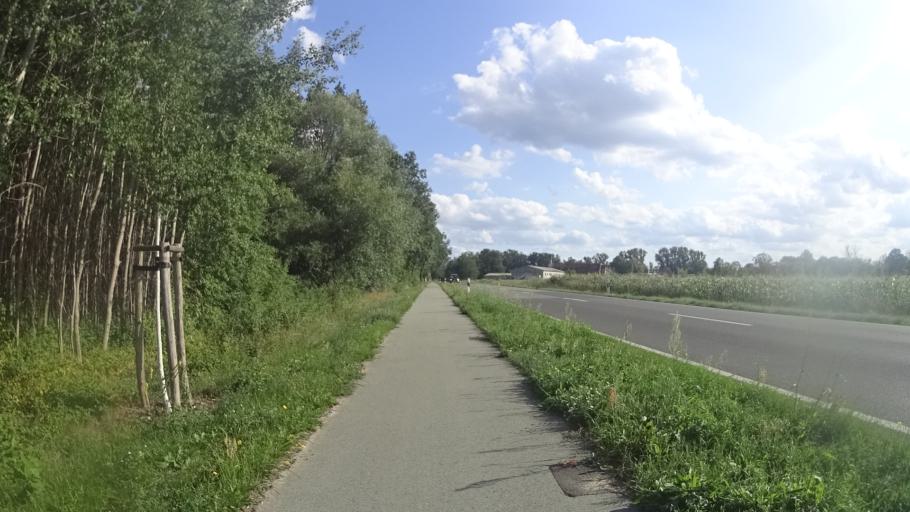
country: DE
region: Brandenburg
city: Rathenow
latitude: 52.6576
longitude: 12.3367
